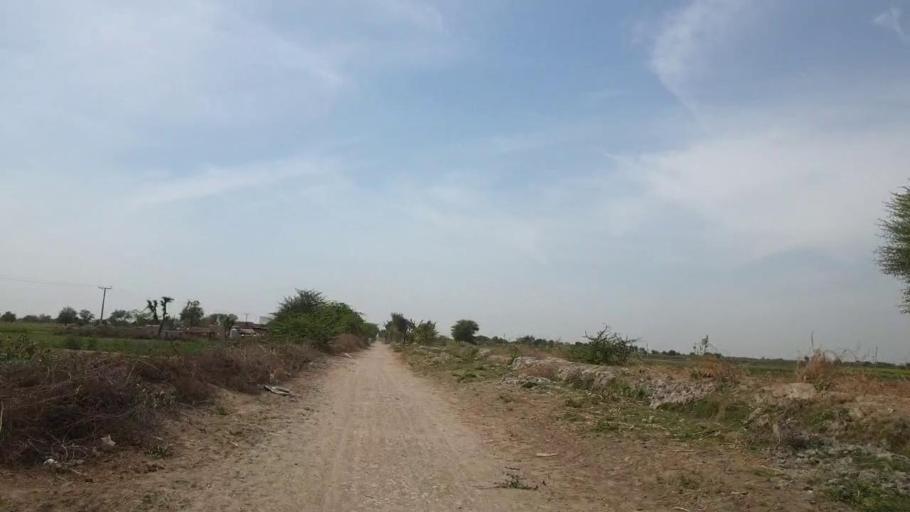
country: PK
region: Sindh
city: Kunri
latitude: 25.1945
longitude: 69.5804
